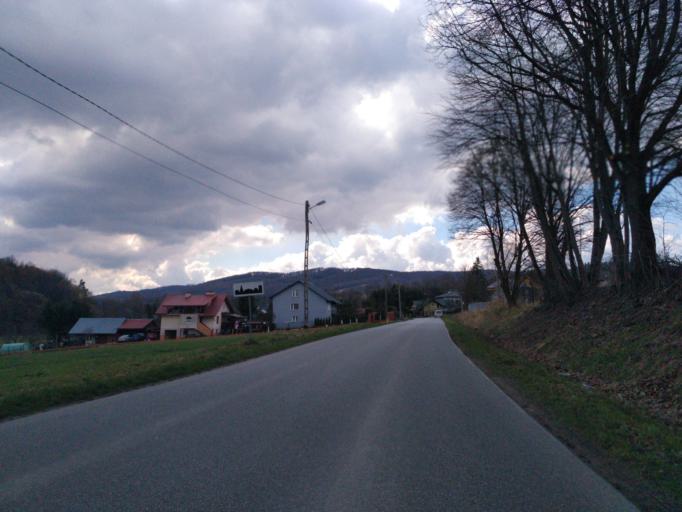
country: PL
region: Subcarpathian Voivodeship
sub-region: Powiat brzozowski
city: Dydnia
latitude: 49.6800
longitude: 22.1842
